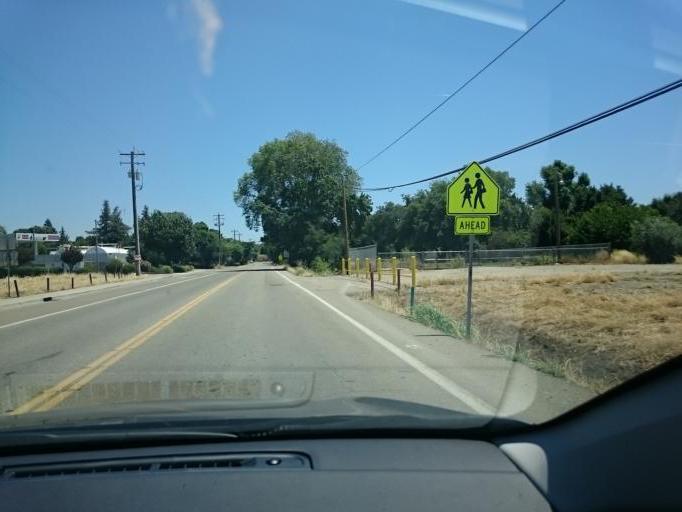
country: US
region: California
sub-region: San Joaquin County
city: Thornton
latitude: 38.2261
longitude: -121.4281
